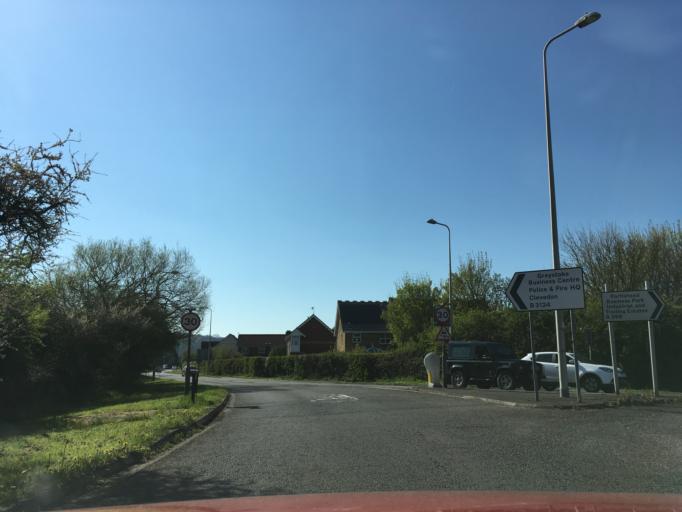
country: GB
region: England
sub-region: North Somerset
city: Portishead
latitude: 51.4774
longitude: -2.7551
